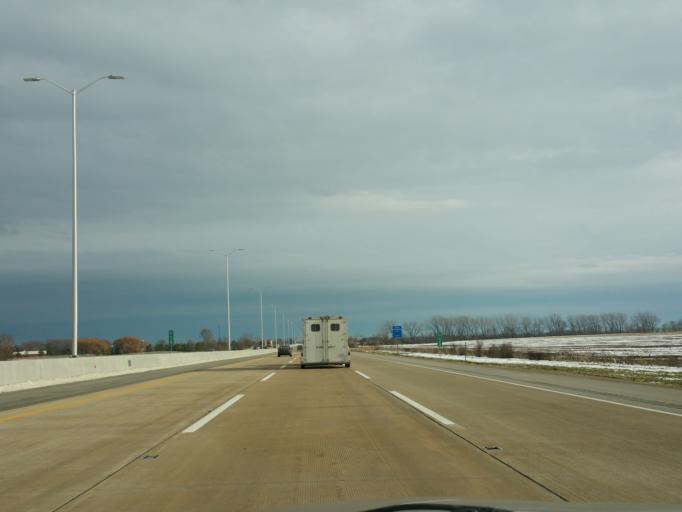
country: US
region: Illinois
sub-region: Boone County
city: Belvidere
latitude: 42.2186
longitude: -88.7466
